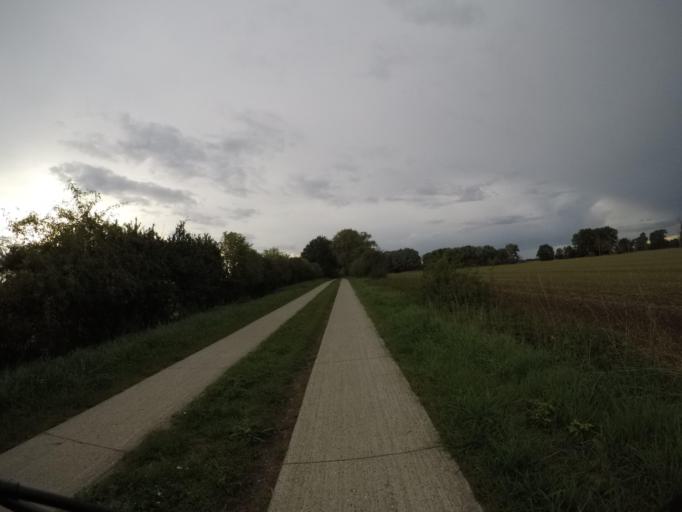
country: DE
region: Lower Saxony
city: Neu Darchau
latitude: 53.2661
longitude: 10.8782
